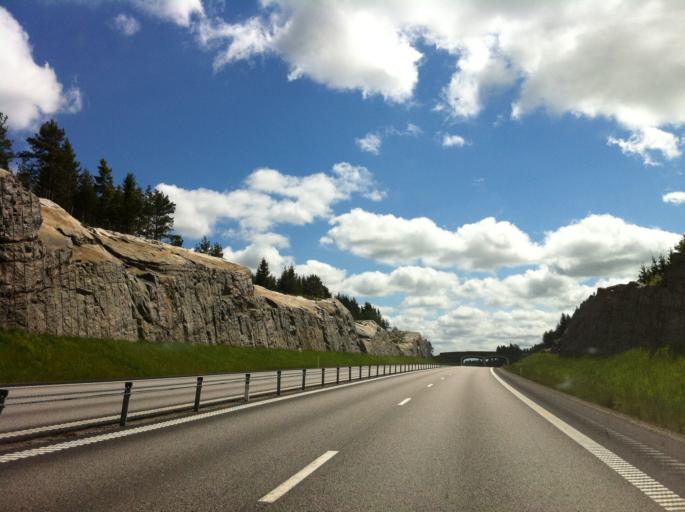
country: SE
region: Vaestra Goetaland
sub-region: Lilla Edets Kommun
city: Lodose
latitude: 58.0578
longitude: 12.1675
